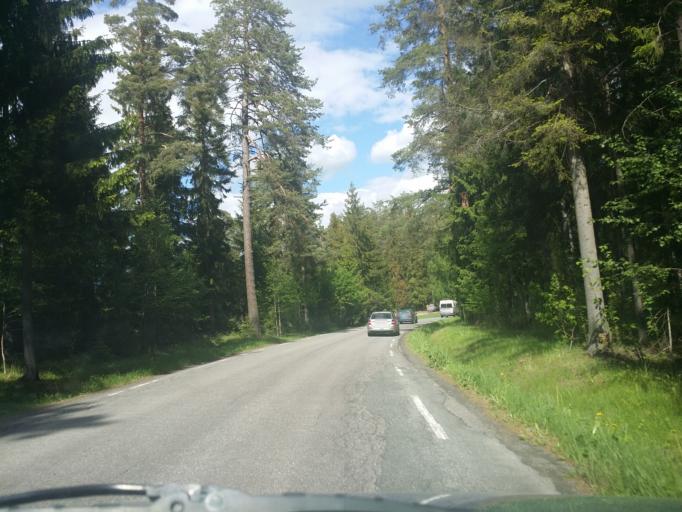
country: NO
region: Oppland
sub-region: Jevnaker
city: Jevnaker
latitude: 60.2325
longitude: 10.3980
